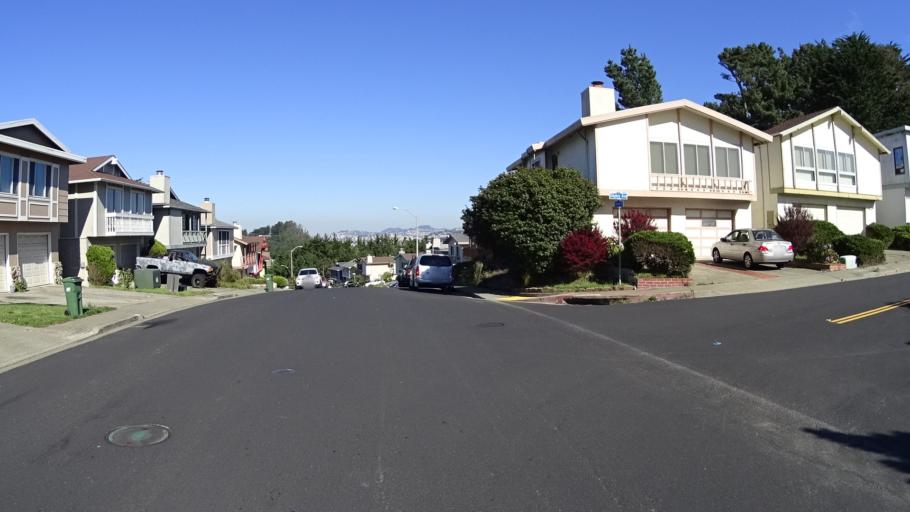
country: US
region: California
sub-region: San Mateo County
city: Colma
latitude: 37.6580
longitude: -122.4694
